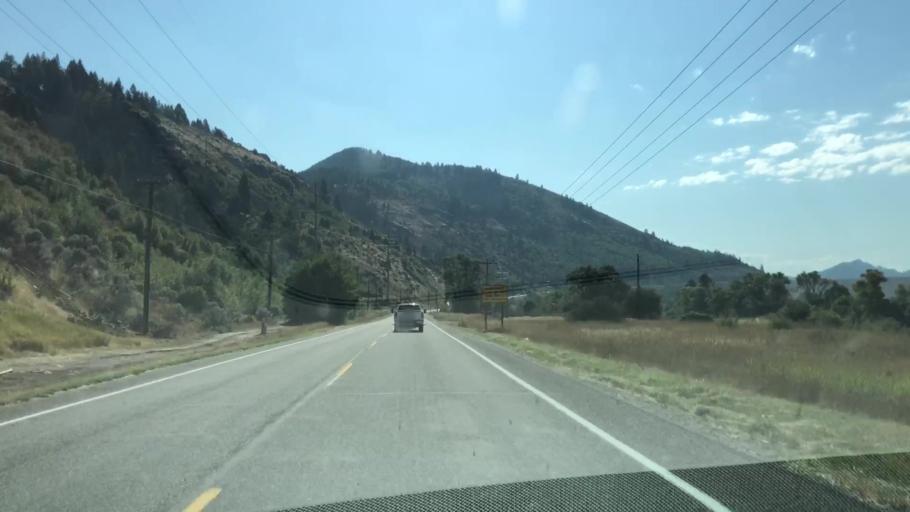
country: US
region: Idaho
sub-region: Teton County
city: Victor
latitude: 43.3484
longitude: -111.2135
